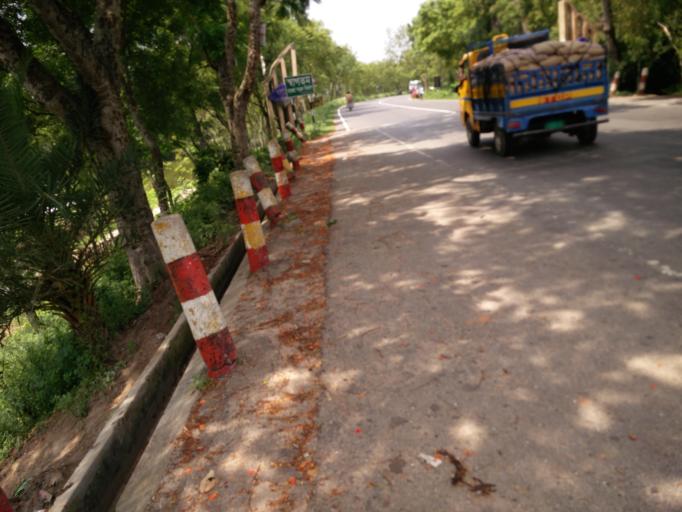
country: BD
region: Khulna
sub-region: Magura
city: Magura
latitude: 23.5392
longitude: 89.5159
